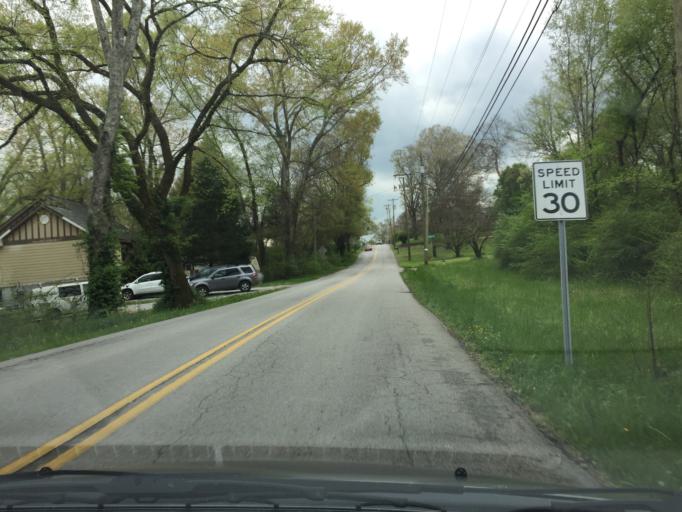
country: US
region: Tennessee
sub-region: Hamilton County
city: Falling Water
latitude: 35.1476
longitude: -85.2383
